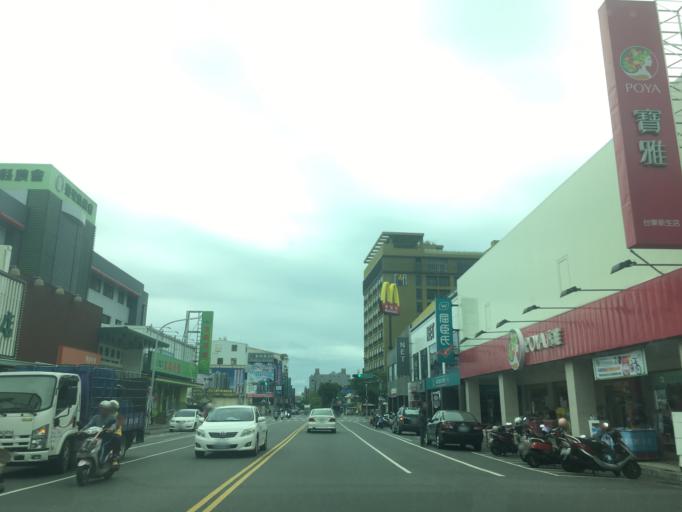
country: TW
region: Taiwan
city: Taitung City
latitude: 22.7559
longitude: 121.1444
